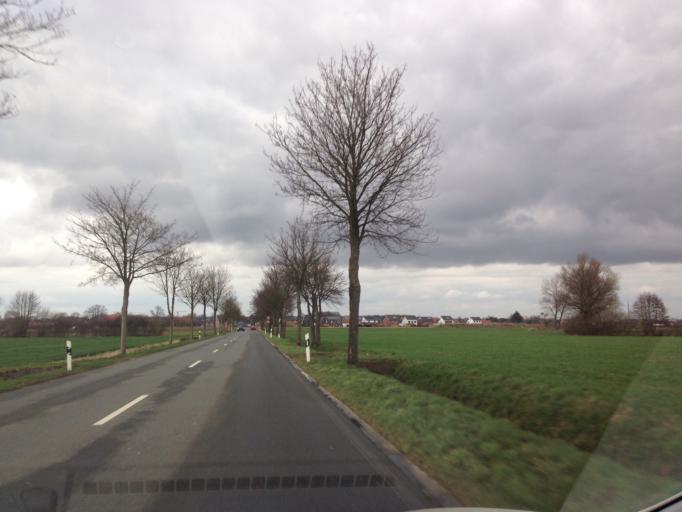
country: DE
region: North Rhine-Westphalia
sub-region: Regierungsbezirk Munster
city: Senden
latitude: 51.8139
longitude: 7.5389
